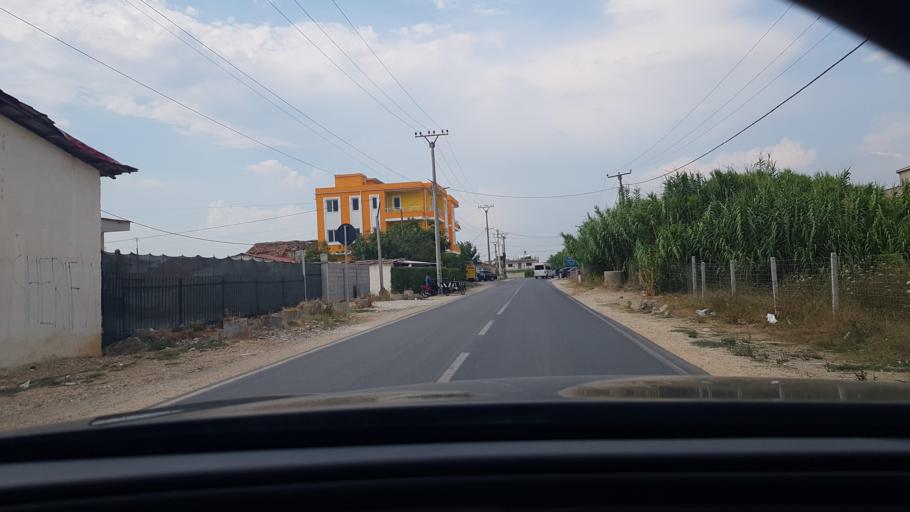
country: AL
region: Durres
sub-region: Rrethi i Durresit
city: Katundi i Ri
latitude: 41.4251
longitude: 19.5480
